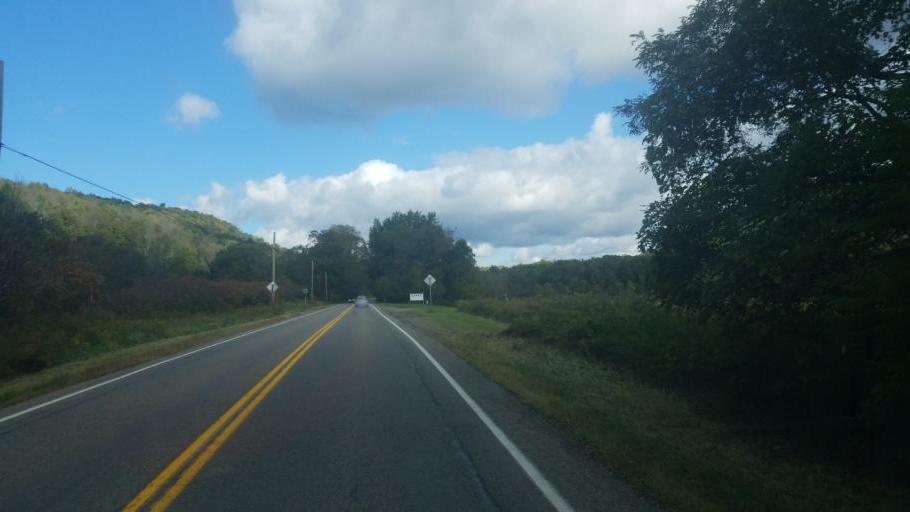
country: US
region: New York
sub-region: Allegany County
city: Cuba
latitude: 42.2191
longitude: -78.3112
